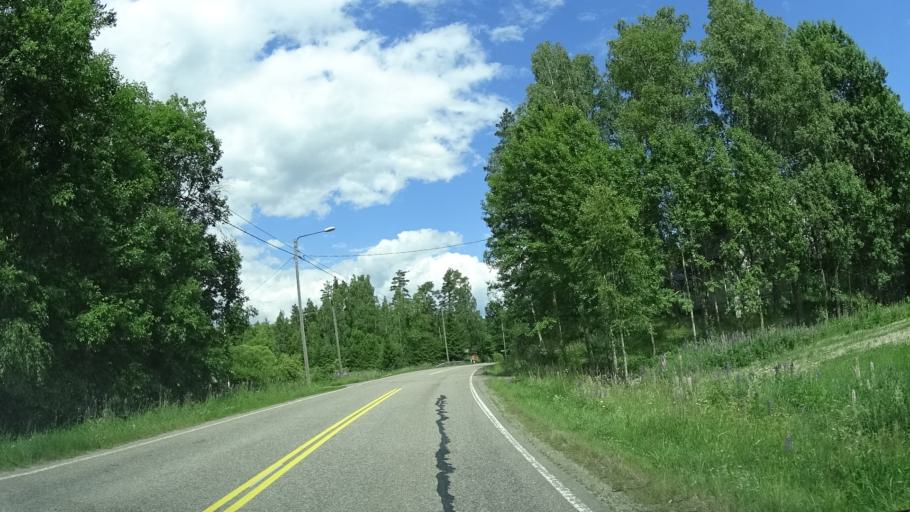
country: FI
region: Uusimaa
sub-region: Helsinki
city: Espoo
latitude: 60.3740
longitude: 24.6403
